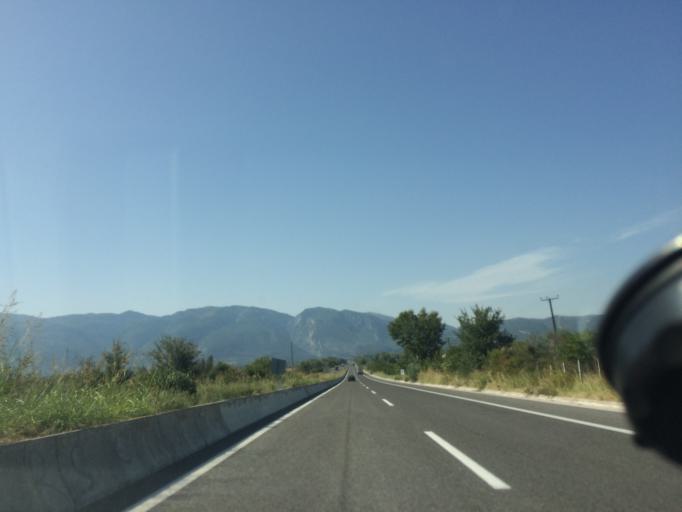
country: GR
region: Thessaly
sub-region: Nomos Larisis
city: Pyrgetos
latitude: 39.9360
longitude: 22.6457
